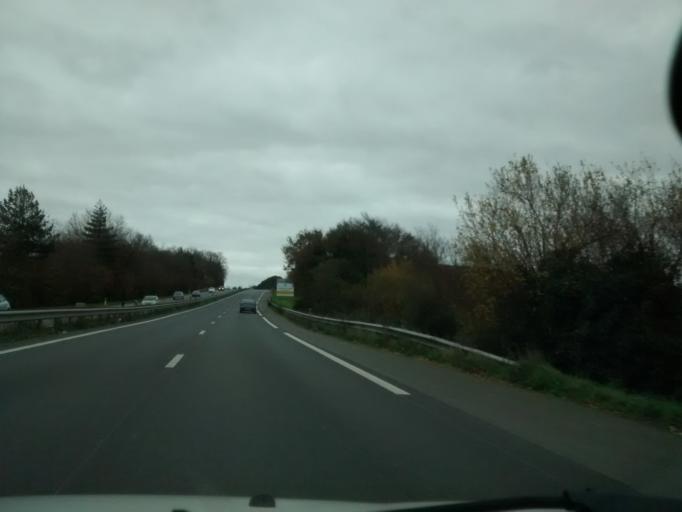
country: FR
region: Brittany
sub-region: Departement d'Ille-et-Vilaine
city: Saint-Pere
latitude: 48.5710
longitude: -1.9331
